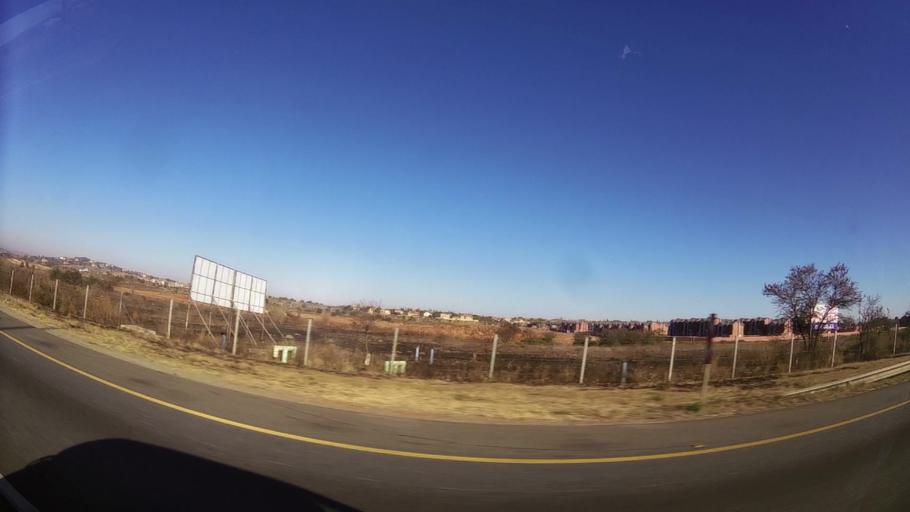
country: ZA
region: Gauteng
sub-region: City of Tshwane Metropolitan Municipality
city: Centurion
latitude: -25.8531
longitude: 28.2517
